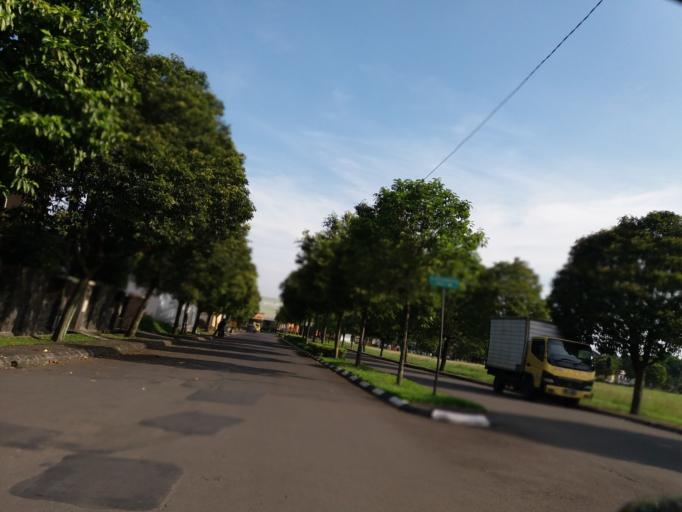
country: ID
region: West Java
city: Bandung
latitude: -6.9617
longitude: 107.6273
